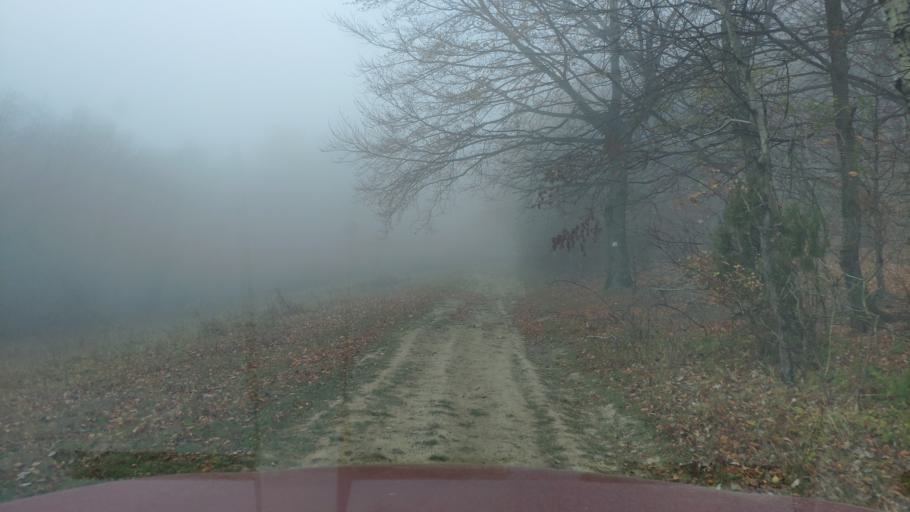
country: SK
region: Presovsky
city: Sabinov
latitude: 49.1511
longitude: 21.2292
